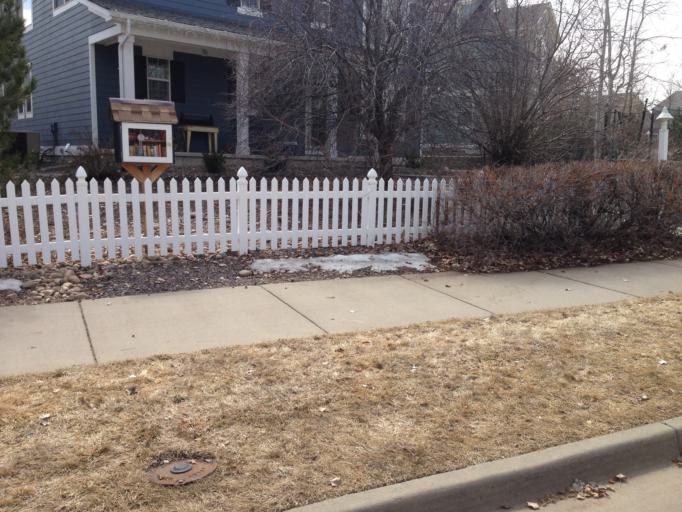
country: US
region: Colorado
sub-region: Boulder County
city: Louisville
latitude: 40.0072
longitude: -105.1393
